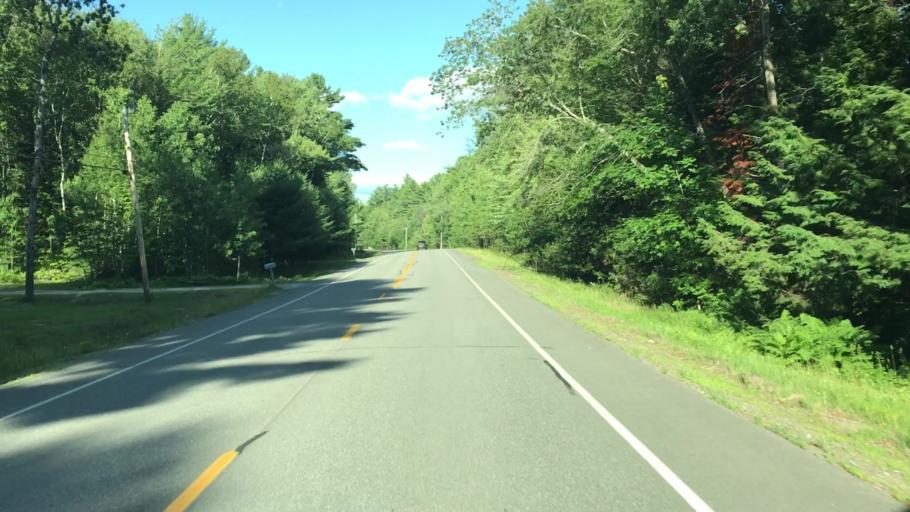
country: US
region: Maine
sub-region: Penobscot County
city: Lincoln
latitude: 45.3788
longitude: -68.4416
